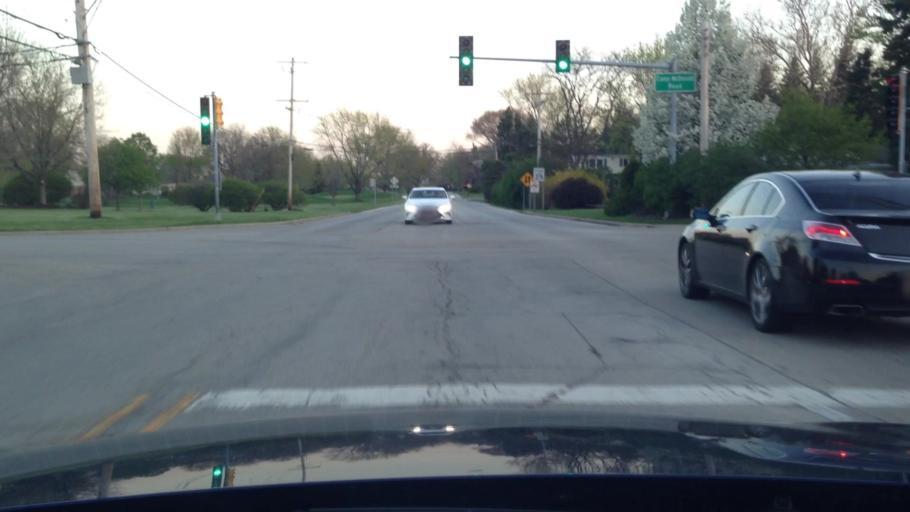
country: US
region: Illinois
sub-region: Cook County
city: Prospect Heights
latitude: 42.0955
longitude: -87.9272
